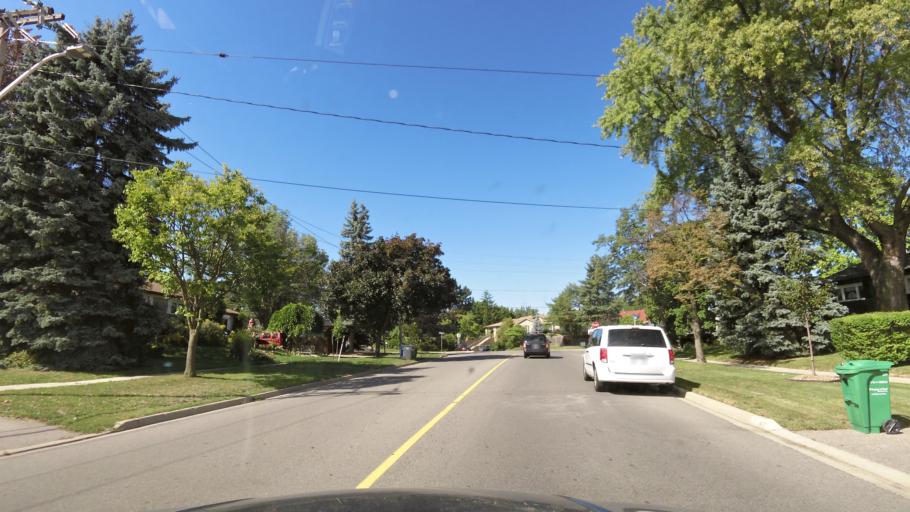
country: CA
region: Ontario
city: Mississauga
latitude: 43.5627
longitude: -79.6686
